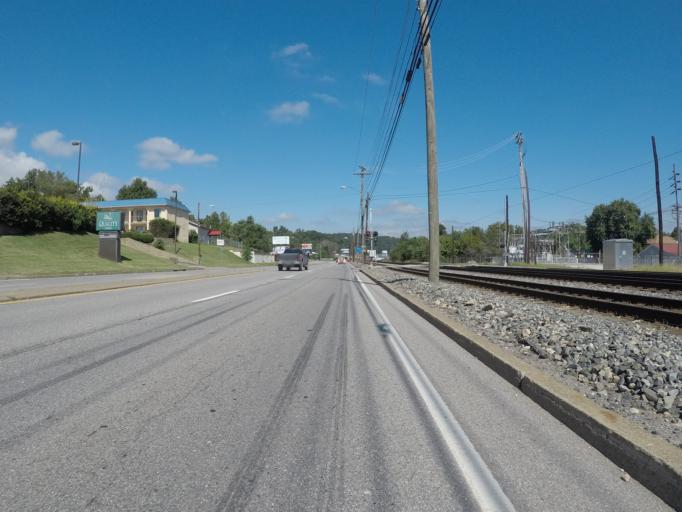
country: US
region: Ohio
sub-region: Lawrence County
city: South Point
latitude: 38.4459
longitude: -82.6111
